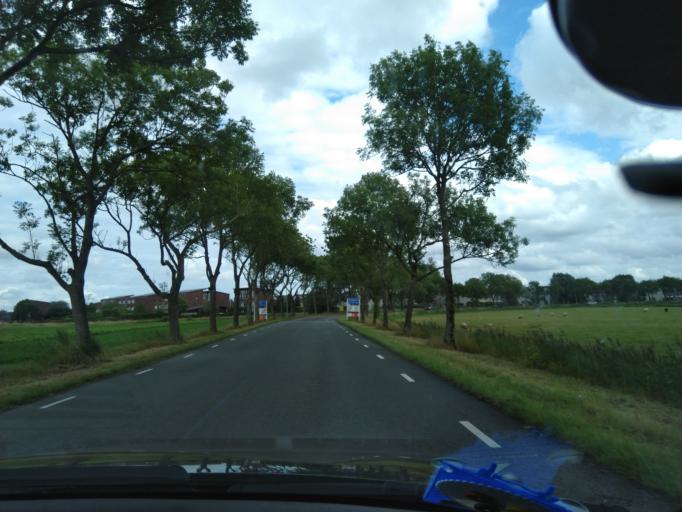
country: NL
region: Groningen
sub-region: Gemeente Zuidhorn
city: Aduard
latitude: 53.2362
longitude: 6.4972
